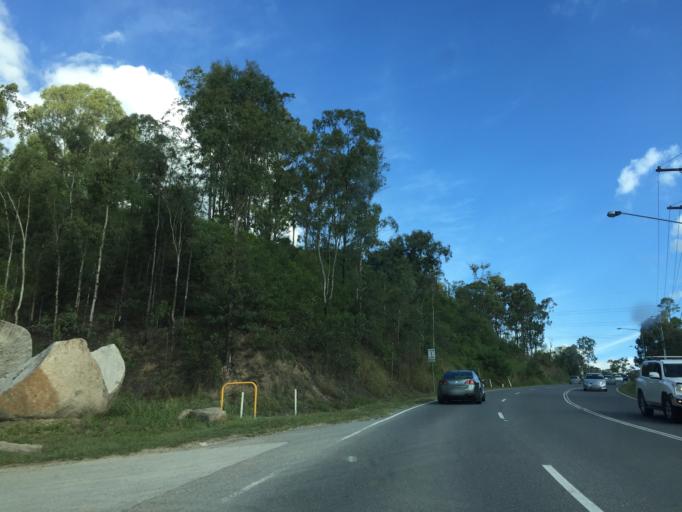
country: AU
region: Queensland
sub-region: Moreton Bay
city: Ferny Hills
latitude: -27.4247
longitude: 152.9492
